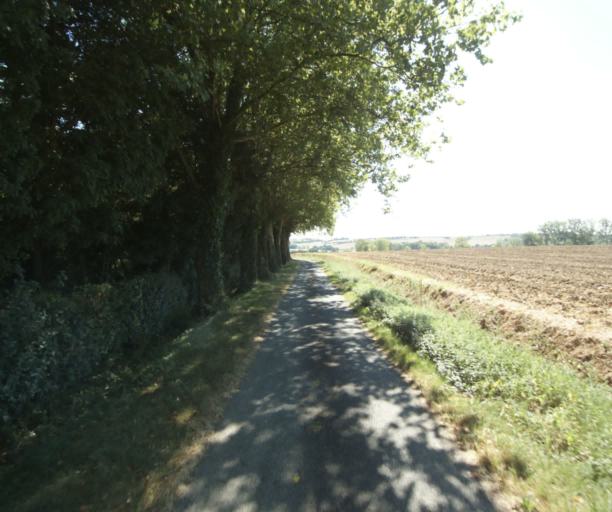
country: FR
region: Midi-Pyrenees
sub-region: Departement de la Haute-Garonne
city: Saint-Felix-Lauragais
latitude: 43.5146
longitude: 1.9008
